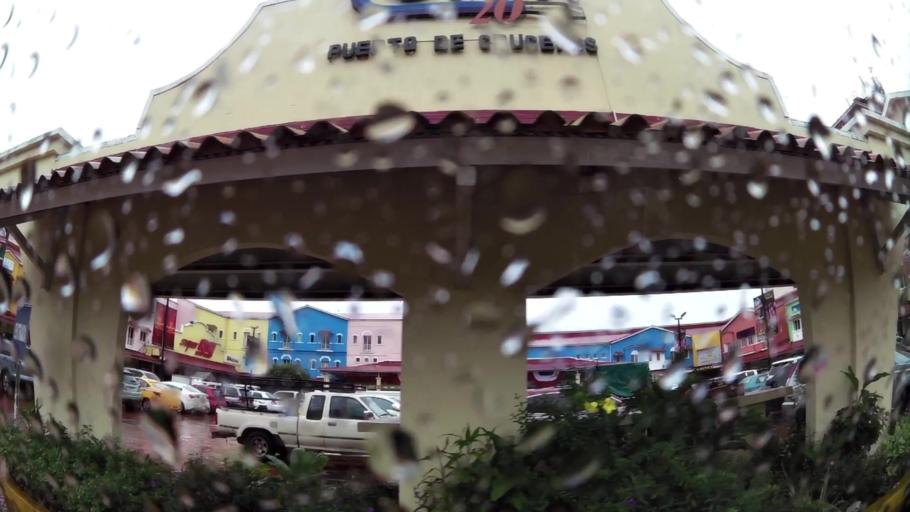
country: PA
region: Colon
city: Colon
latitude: 9.3572
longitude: -79.8925
